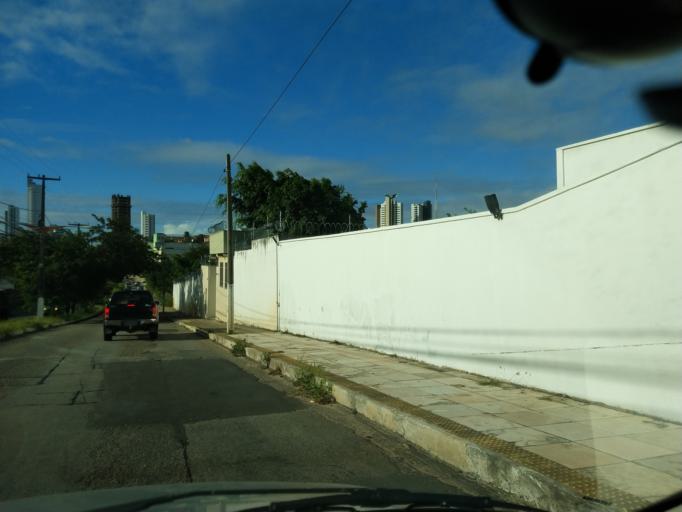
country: BR
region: Rio Grande do Norte
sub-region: Natal
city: Natal
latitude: -5.8342
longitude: -35.2240
